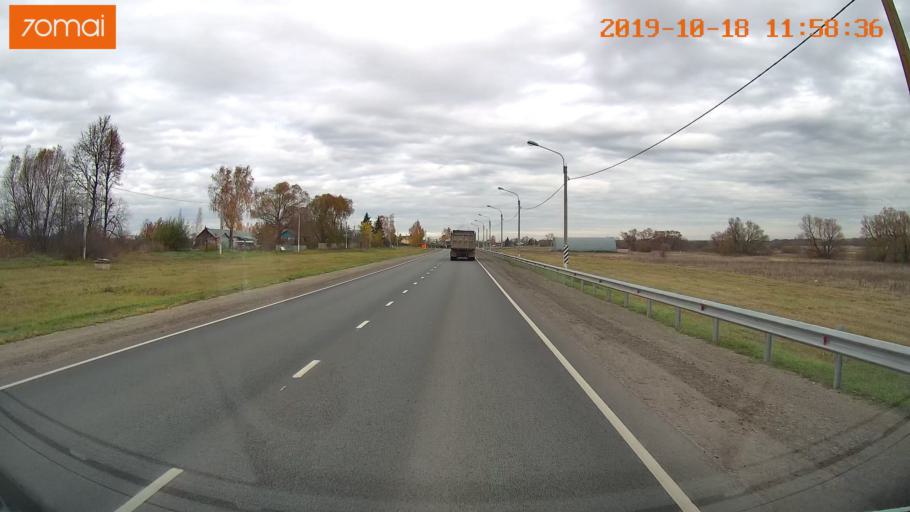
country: RU
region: Rjazan
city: Zakharovo
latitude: 54.2735
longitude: 39.1684
